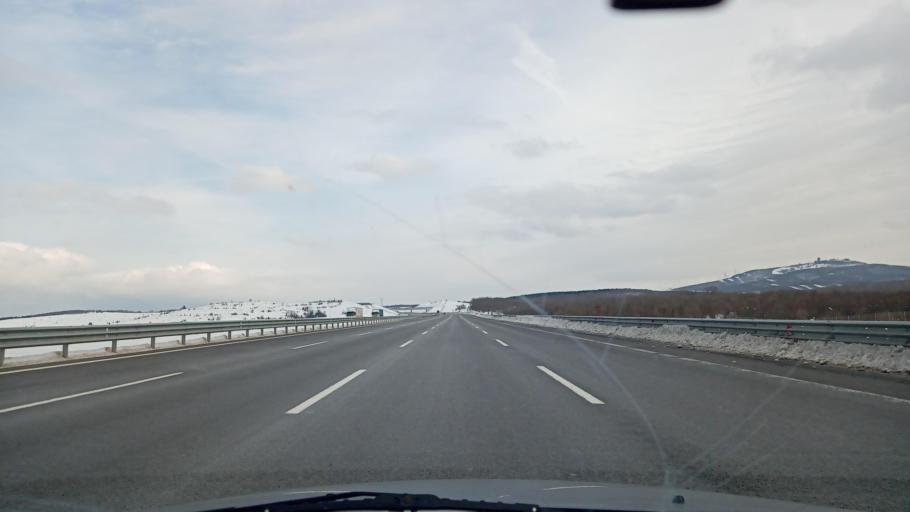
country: TR
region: Kocaeli
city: Hereke
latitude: 40.8934
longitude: 29.6127
